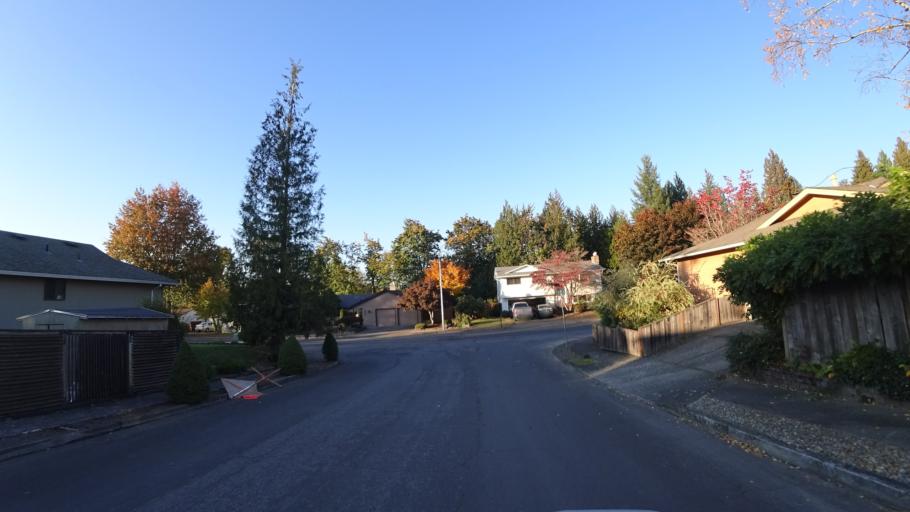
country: US
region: Oregon
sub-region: Multnomah County
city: Gresham
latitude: 45.4944
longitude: -122.4360
